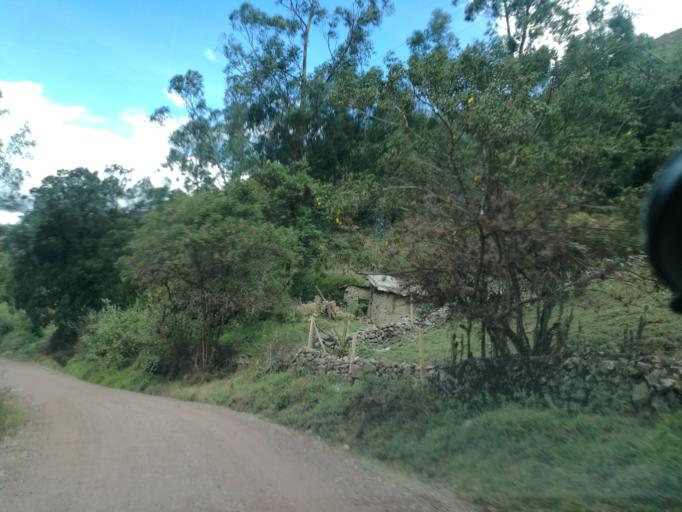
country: CO
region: Boyaca
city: Susacon
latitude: 6.1251
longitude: -72.7112
